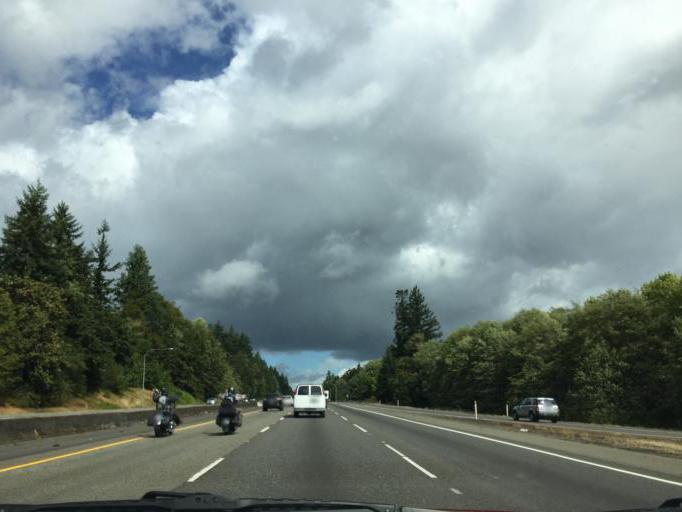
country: US
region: Washington
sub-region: Lewis County
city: Winlock
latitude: 46.4783
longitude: -122.8821
